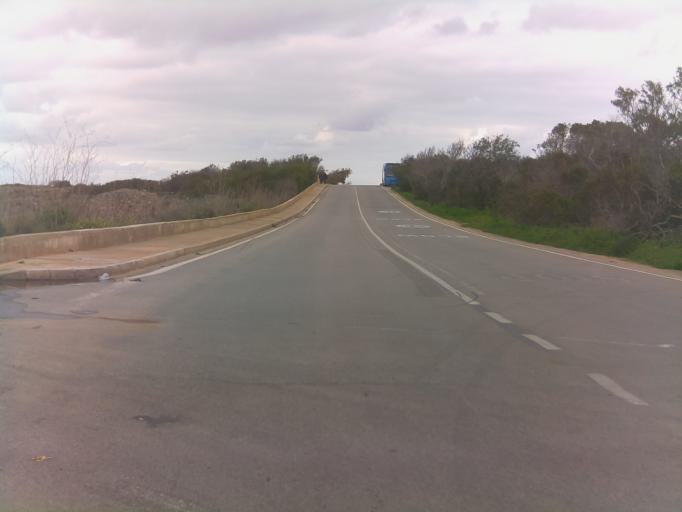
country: MT
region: Il-Mellieha
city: Mellieha
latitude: 35.9773
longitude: 14.3490
